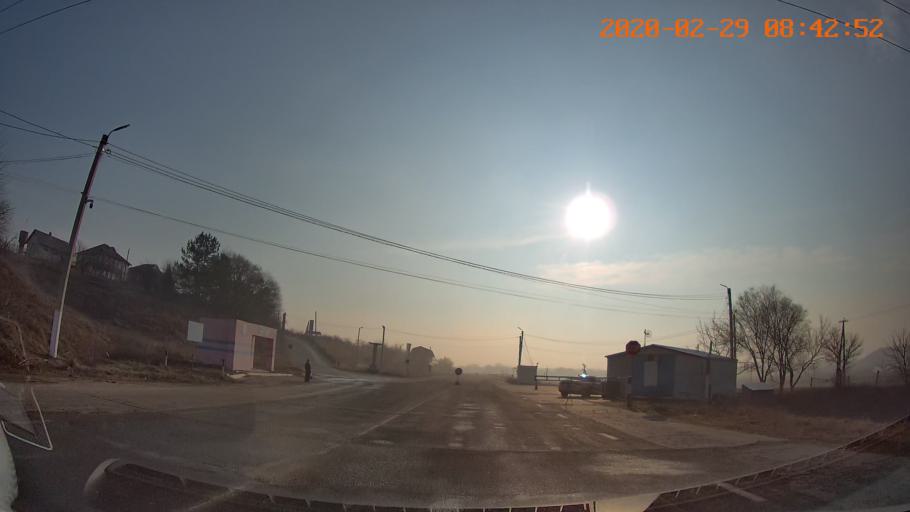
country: MD
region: Anenii Noi
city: Varnita
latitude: 46.9209
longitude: 29.4547
